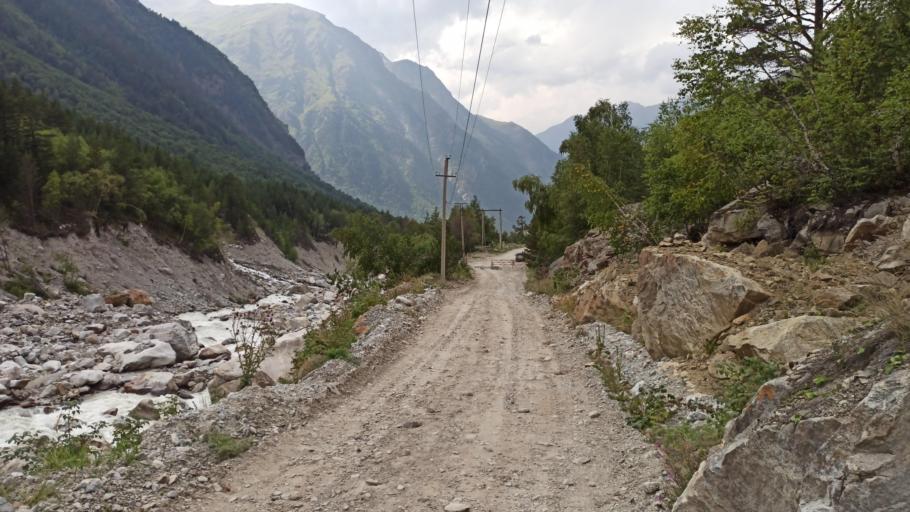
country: RU
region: Kabardino-Balkariya
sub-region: El'brusskiy Rayon
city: El'brus
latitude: 43.2207
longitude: 42.6867
